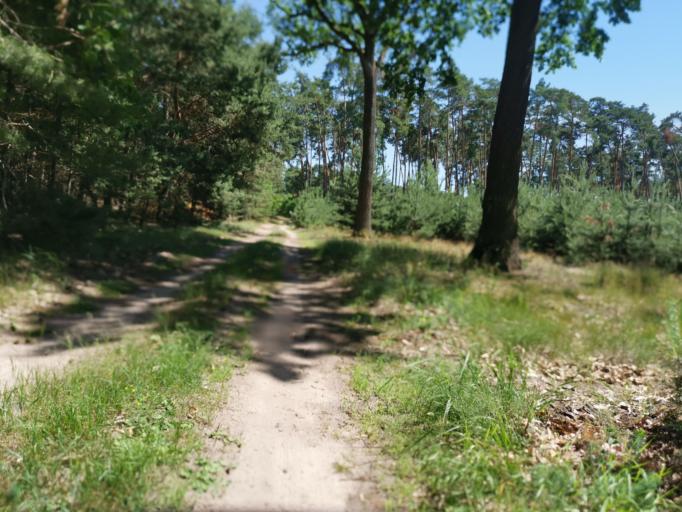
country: CZ
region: South Moravian
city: Bzenec
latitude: 48.9450
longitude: 17.2405
